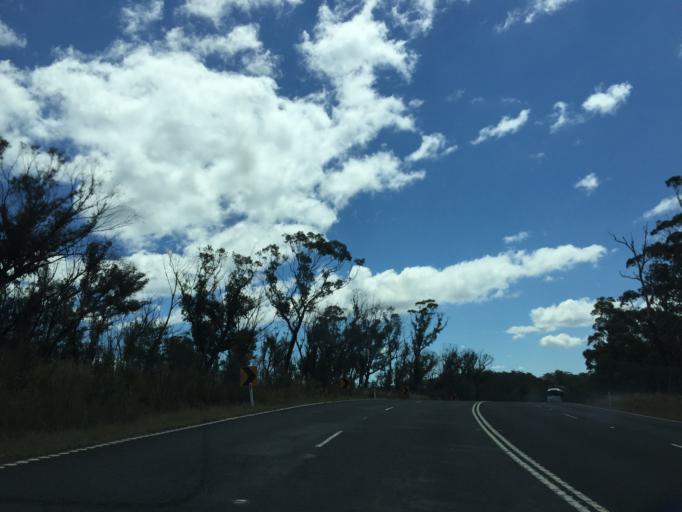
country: AU
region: New South Wales
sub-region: Blue Mountains Municipality
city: Blackheath
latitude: -33.5189
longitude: 150.2954
